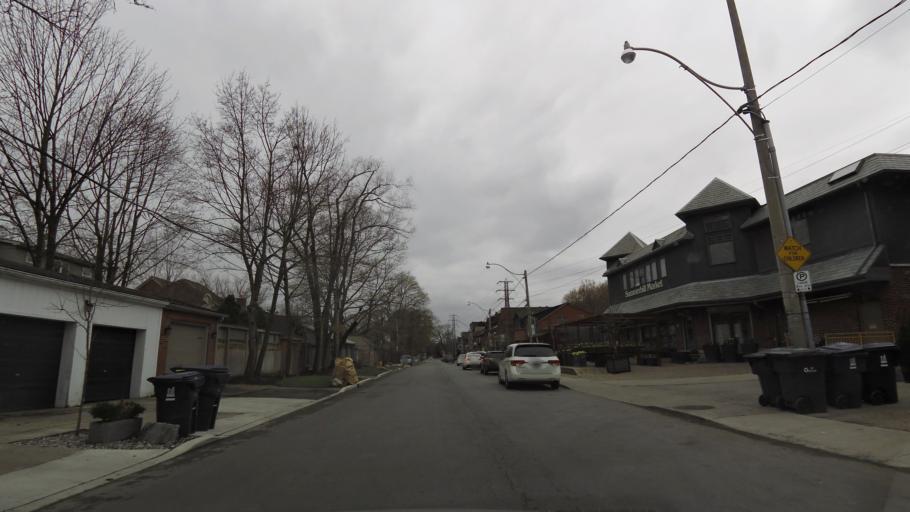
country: CA
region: Ontario
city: Toronto
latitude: 43.6863
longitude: -79.3748
